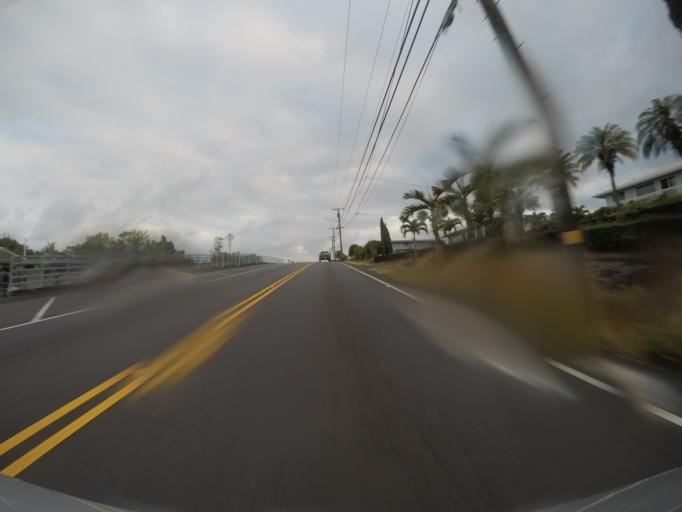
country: US
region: Hawaii
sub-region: Hawaii County
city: Hilo
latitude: 19.6866
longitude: -155.0900
